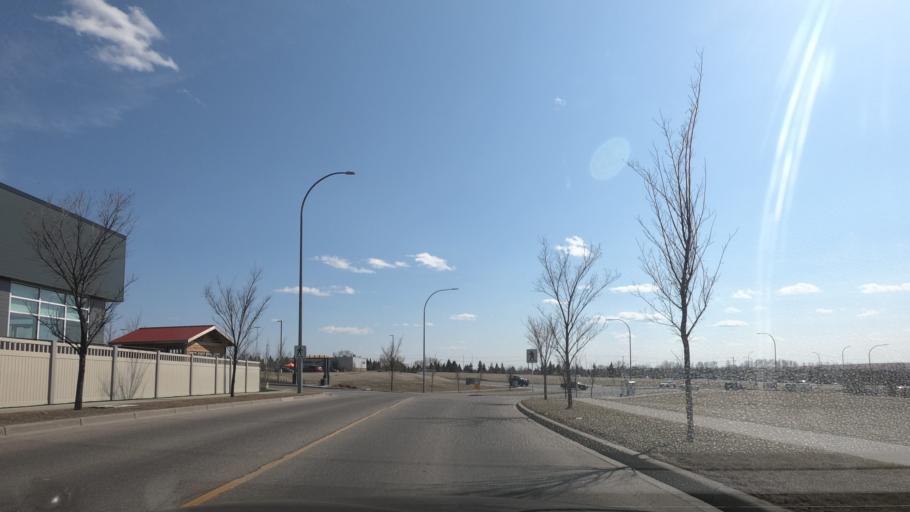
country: CA
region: Alberta
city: Airdrie
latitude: 51.3025
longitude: -114.0113
